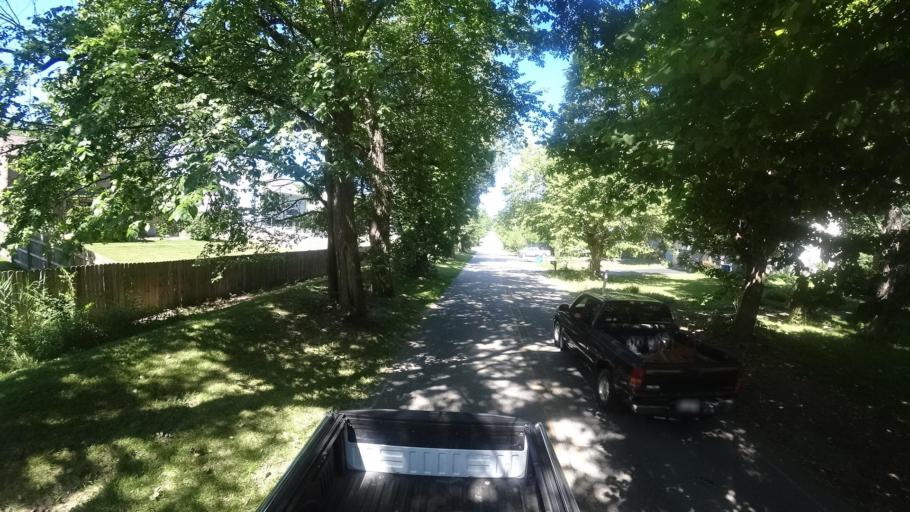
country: US
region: Indiana
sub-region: Porter County
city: Porter
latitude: 41.6296
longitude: -87.0698
